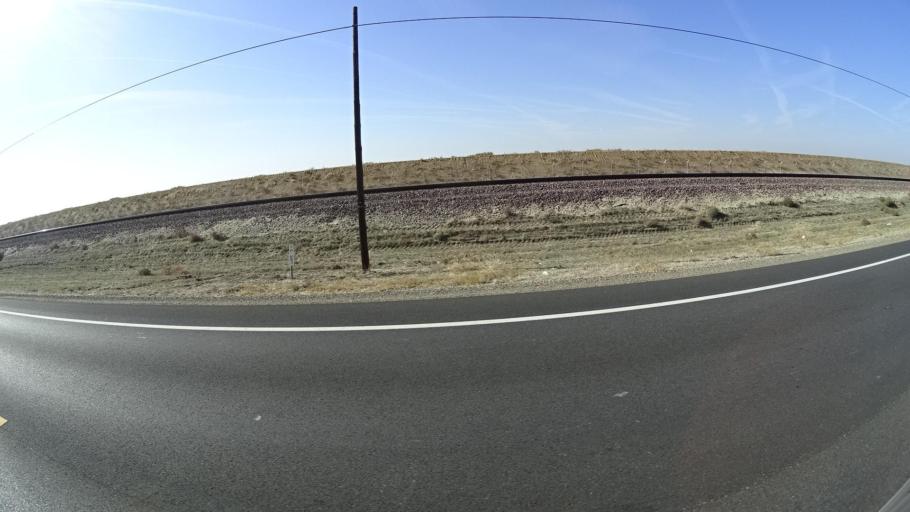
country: US
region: California
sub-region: Kern County
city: Wasco
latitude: 35.6469
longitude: -119.3310
